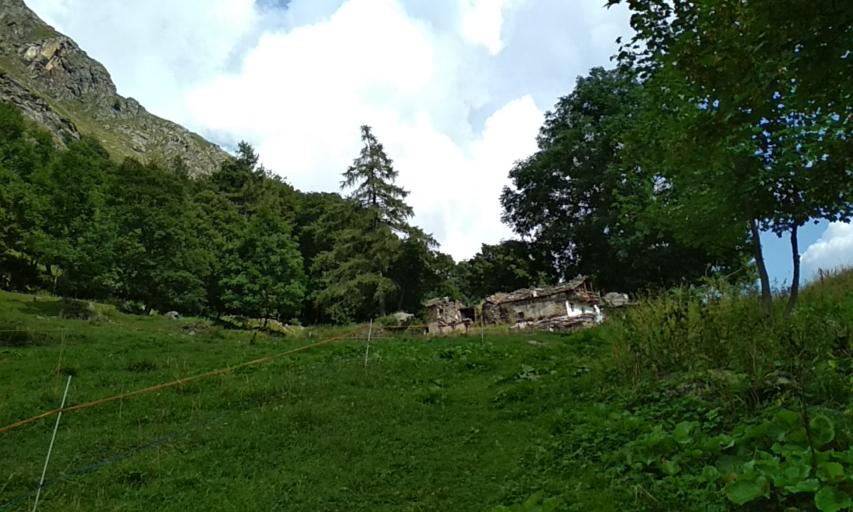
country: IT
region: Piedmont
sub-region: Provincia di Torino
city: Noasca
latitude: 45.4587
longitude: 7.2805
